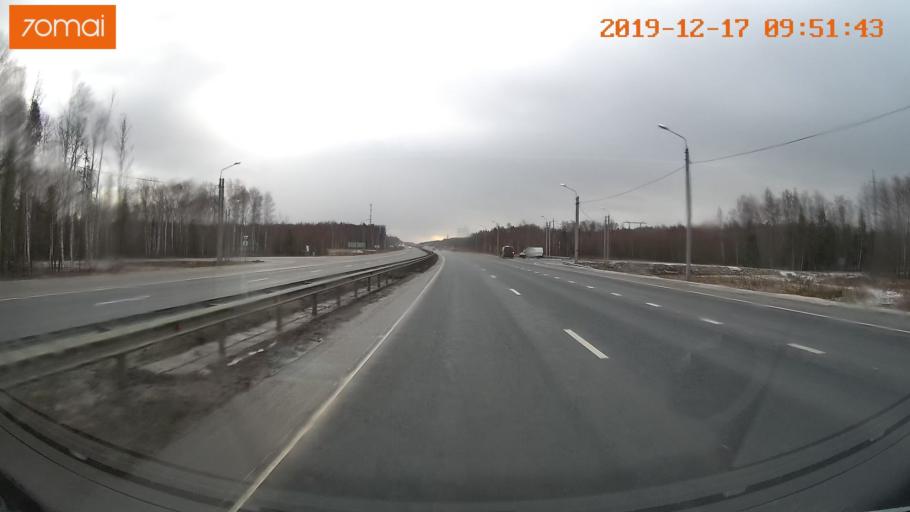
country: RU
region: Vladimir
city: Kommunar
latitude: 56.0407
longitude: 40.5253
